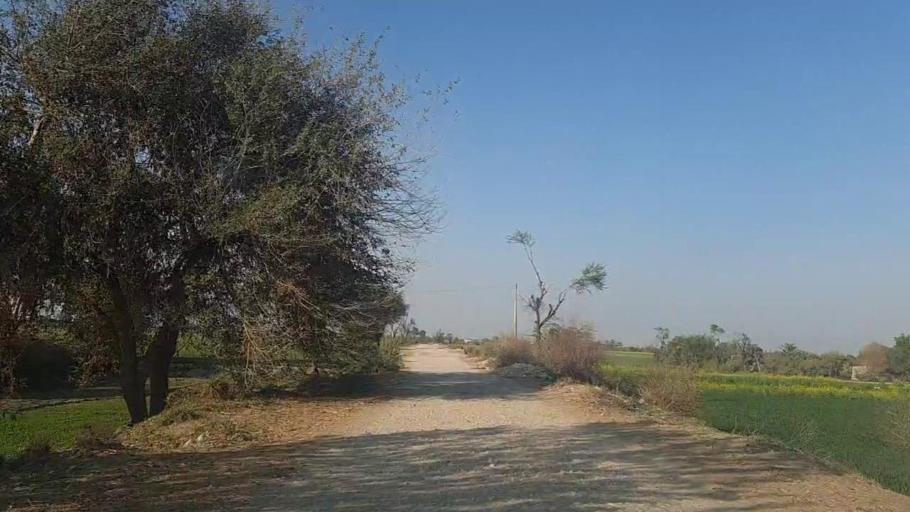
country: PK
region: Sindh
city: Jam Sahib
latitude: 26.3128
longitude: 68.7150
